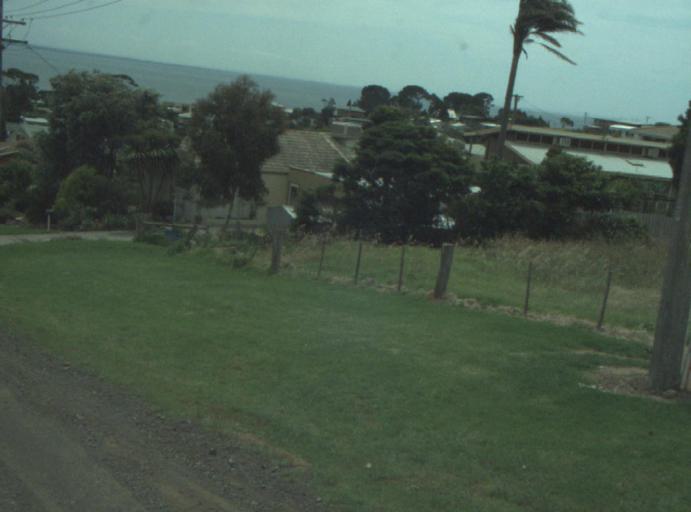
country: AU
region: Victoria
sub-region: Greater Geelong
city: Clifton Springs
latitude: -38.1222
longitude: 144.6454
